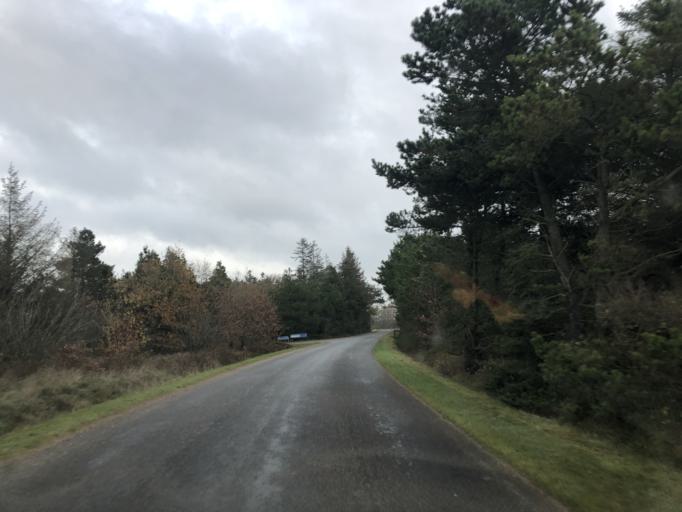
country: DK
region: Central Jutland
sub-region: Holstebro Kommune
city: Ulfborg
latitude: 56.3137
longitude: 8.2162
